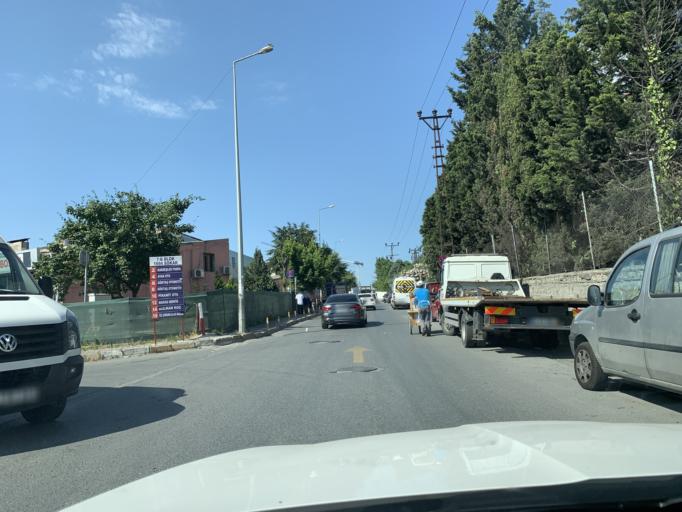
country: TR
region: Istanbul
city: Esenyurt
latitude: 41.0613
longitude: 28.6628
